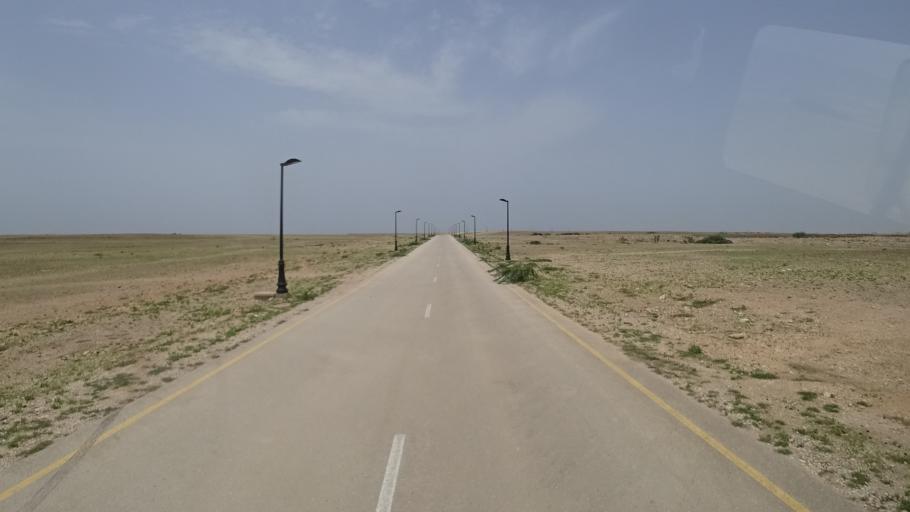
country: OM
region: Zufar
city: Salalah
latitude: 17.0535
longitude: 54.4383
